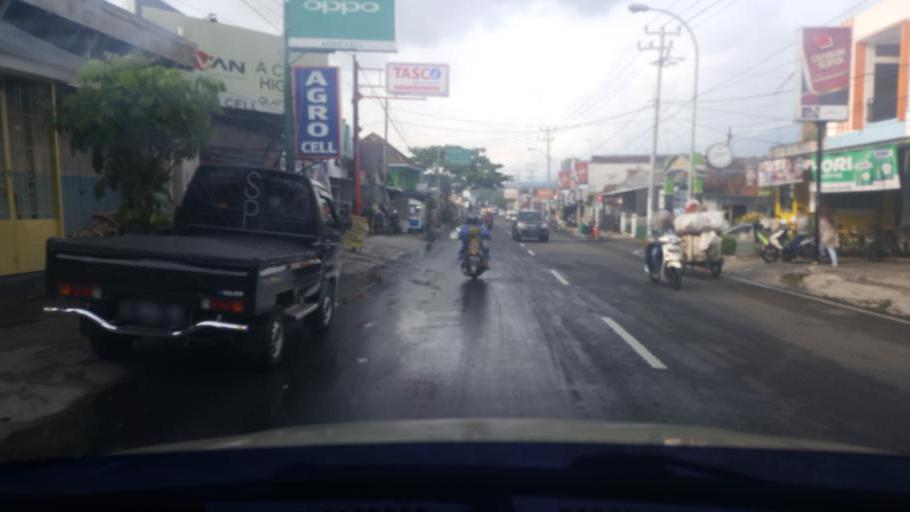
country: ID
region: West Java
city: Pakemitan
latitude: -7.2909
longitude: 108.2003
